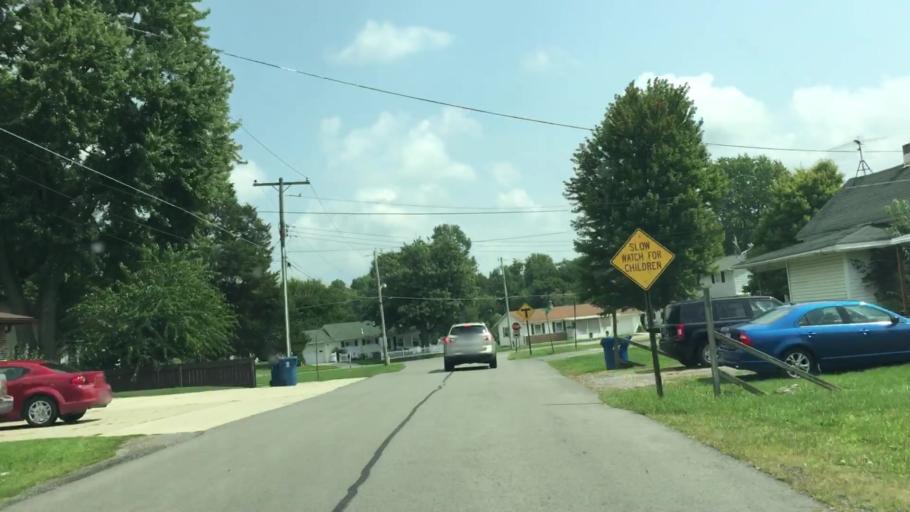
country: US
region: Ohio
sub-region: Logan County
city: Bellefontaine
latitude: 40.3420
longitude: -83.7604
